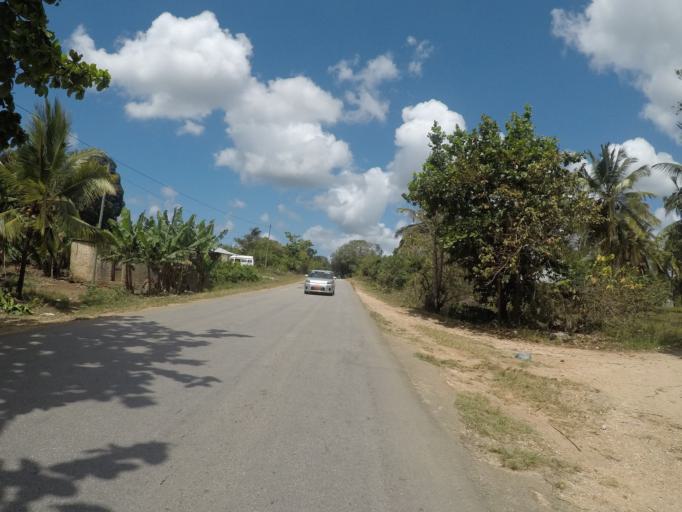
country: TZ
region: Zanzibar Central/South
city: Mahonda
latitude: -6.2851
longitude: 39.4110
